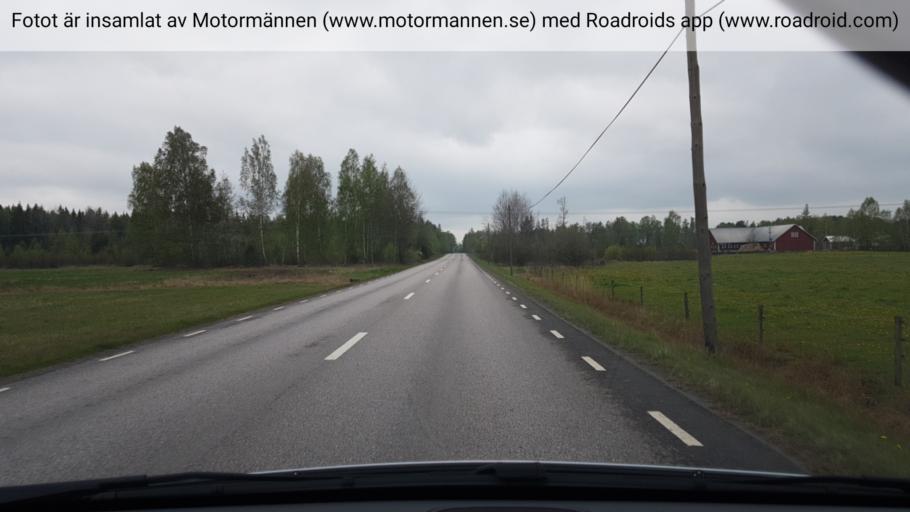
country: SE
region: Vaestra Goetaland
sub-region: Skovde Kommun
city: Stopen
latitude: 58.5269
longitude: 13.9888
